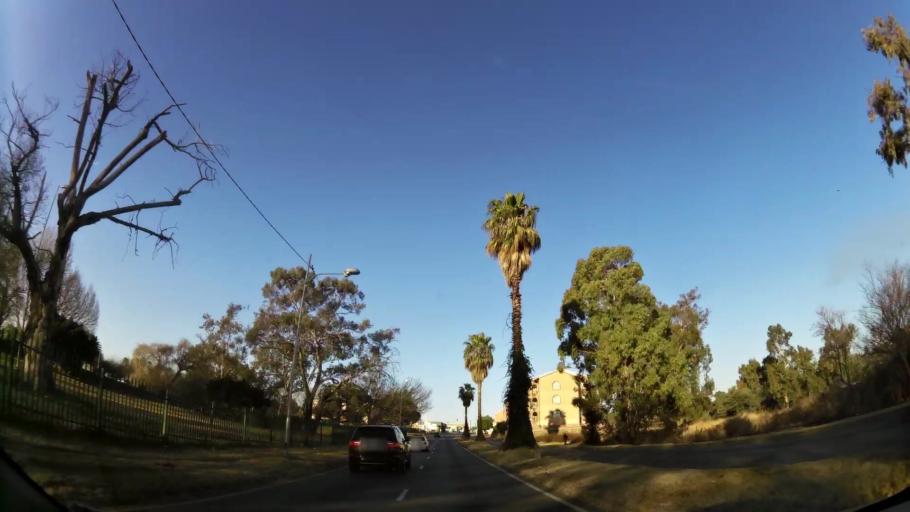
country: ZA
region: Gauteng
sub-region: City of Johannesburg Metropolitan Municipality
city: Roodepoort
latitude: -26.1819
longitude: 27.9068
